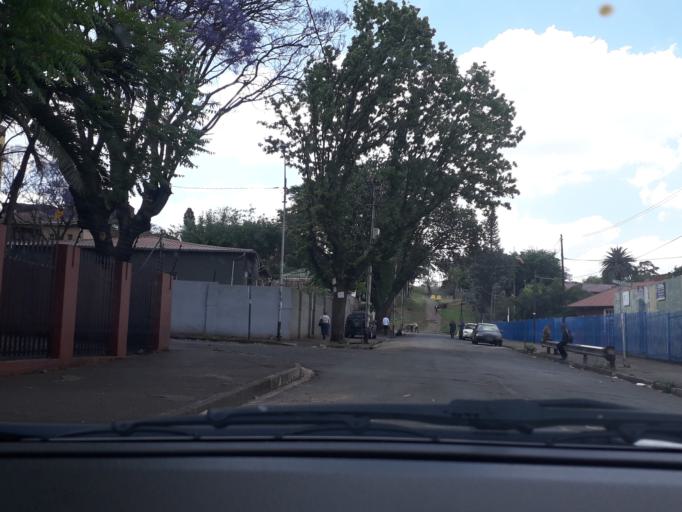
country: ZA
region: Gauteng
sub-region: City of Johannesburg Metropolitan Municipality
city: Johannesburg
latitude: -26.1793
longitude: 28.0721
